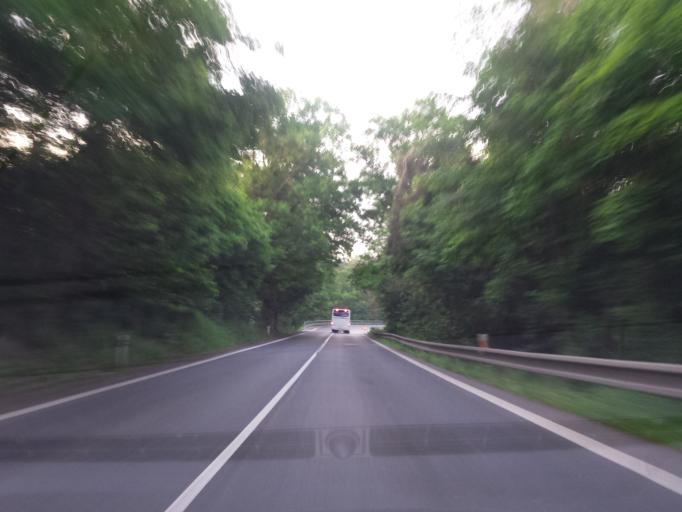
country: CZ
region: Liberecky
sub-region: Okres Ceska Lipa
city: Ceska Lipa
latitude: 50.6330
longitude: 14.5362
